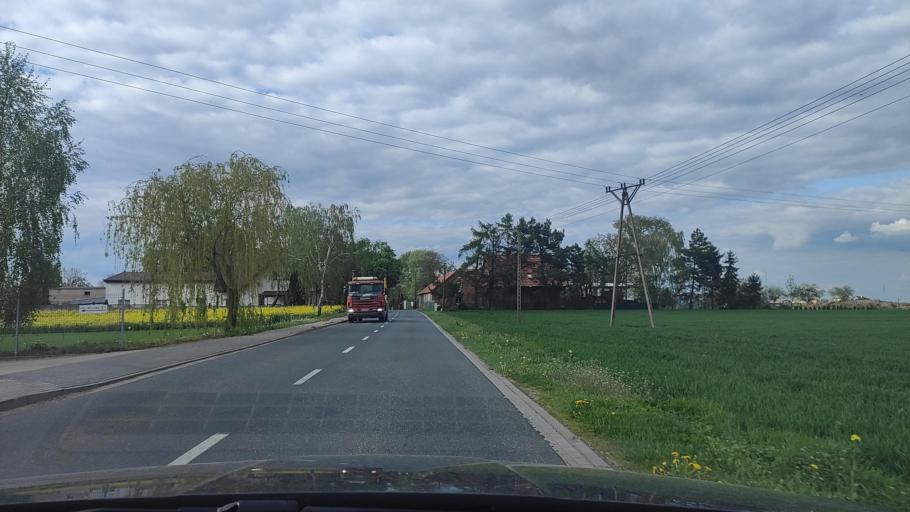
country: PL
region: Greater Poland Voivodeship
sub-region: Powiat poznanski
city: Swarzedz
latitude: 52.4241
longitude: 17.1576
